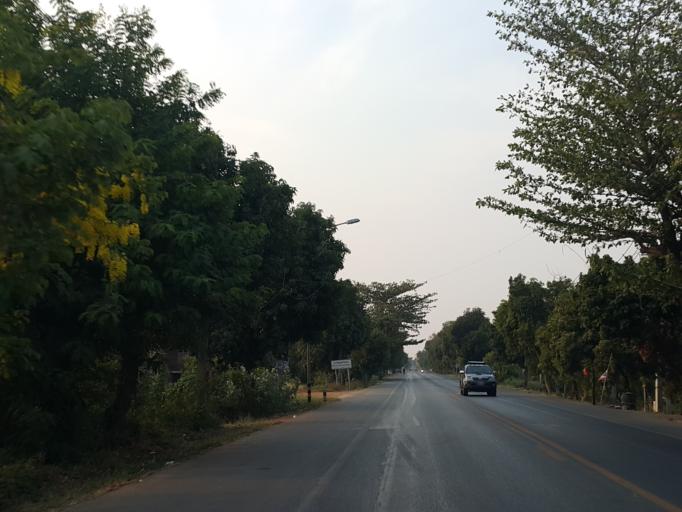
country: TH
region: Sukhothai
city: Si Samrong
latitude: 17.2301
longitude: 99.8582
